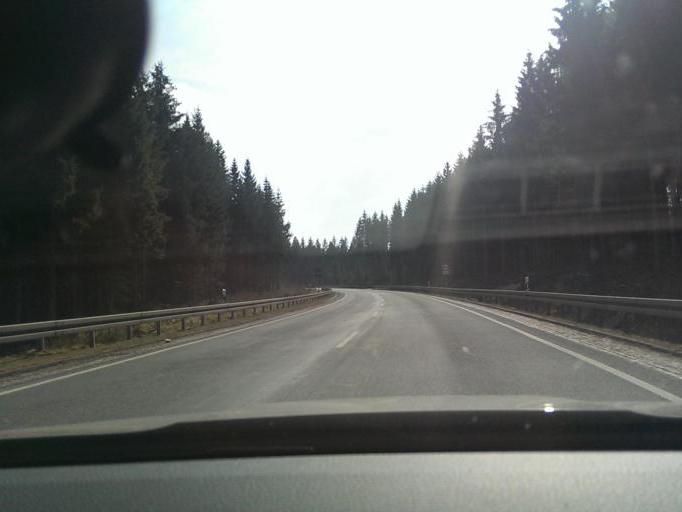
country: DE
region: Thuringia
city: Luisenthal
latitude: 50.7528
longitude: 10.7402
